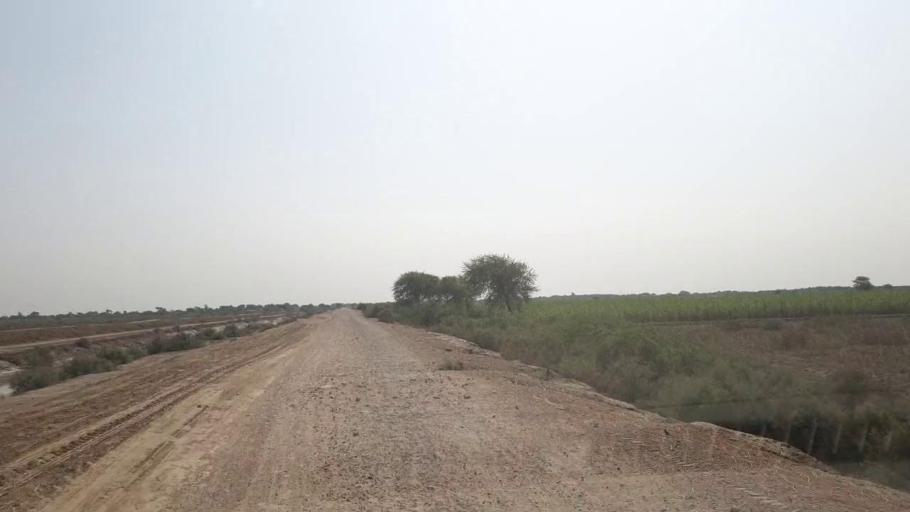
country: PK
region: Sindh
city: Kadhan
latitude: 24.4712
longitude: 68.9038
